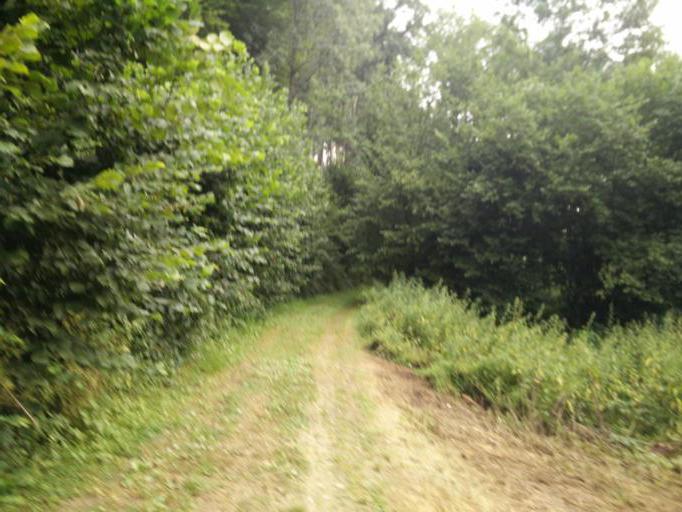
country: LU
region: Luxembourg
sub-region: Canton de Capellen
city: Mamer
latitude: 49.6342
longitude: 6.0456
